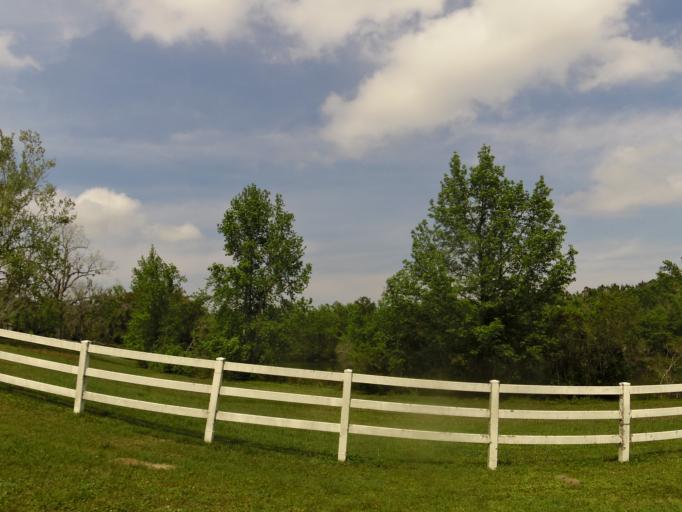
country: US
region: Georgia
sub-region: Camden County
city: Kingsland
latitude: 30.7806
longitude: -81.6885
